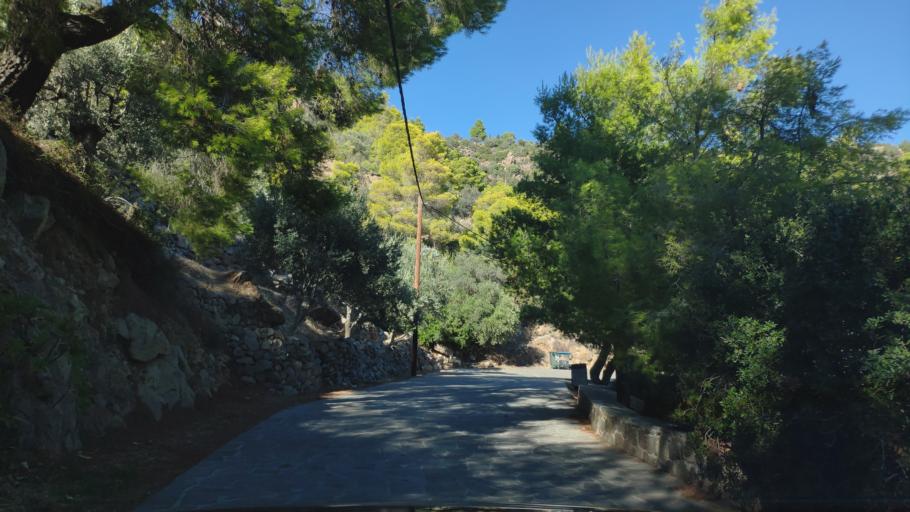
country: GR
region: Attica
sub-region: Nomos Piraios
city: Poros
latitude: 37.5902
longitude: 23.4020
